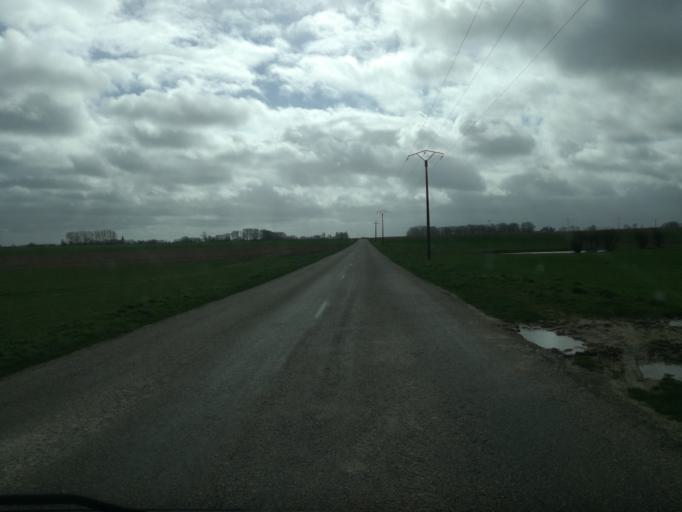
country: FR
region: Haute-Normandie
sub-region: Departement de la Seine-Maritime
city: Valliquerville
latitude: 49.6058
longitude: 0.6669
